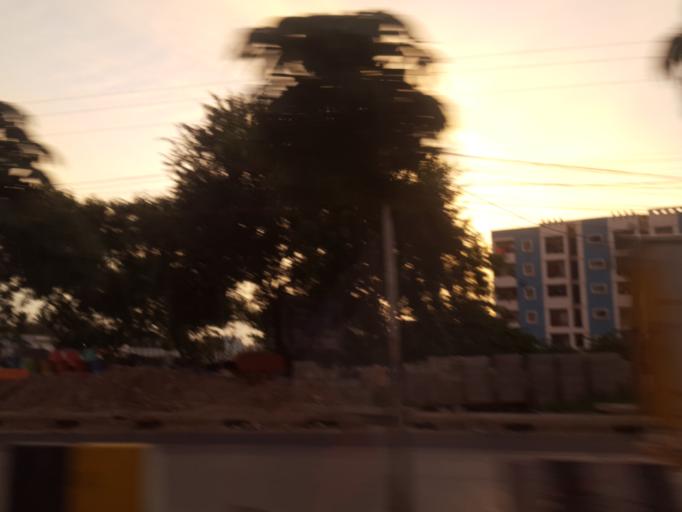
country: IN
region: Telangana
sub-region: Rangareddi
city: Kukatpalli
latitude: 17.5005
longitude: 78.3621
